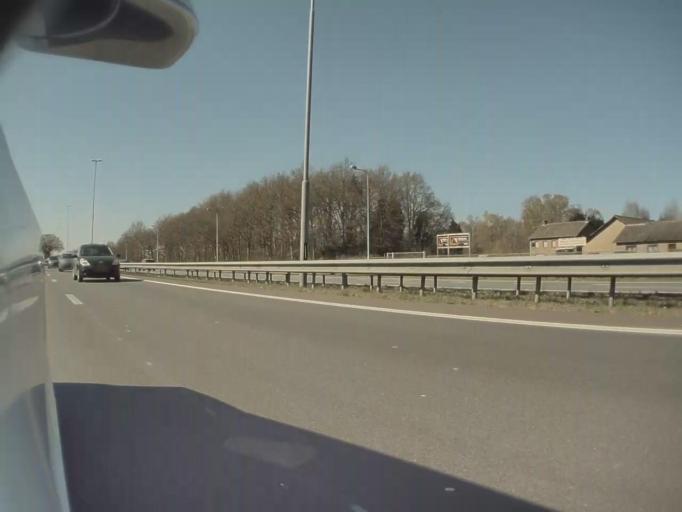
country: NL
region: North Brabant
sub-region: Gemeente Maasdonk
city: Geffen
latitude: 51.7320
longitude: 5.4869
